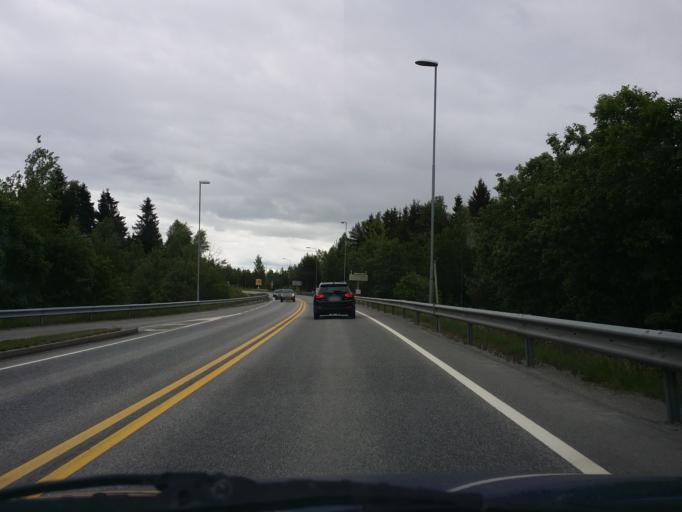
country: NO
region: Hedmark
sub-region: Ringsaker
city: Moelv
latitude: 60.9210
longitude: 10.6952
